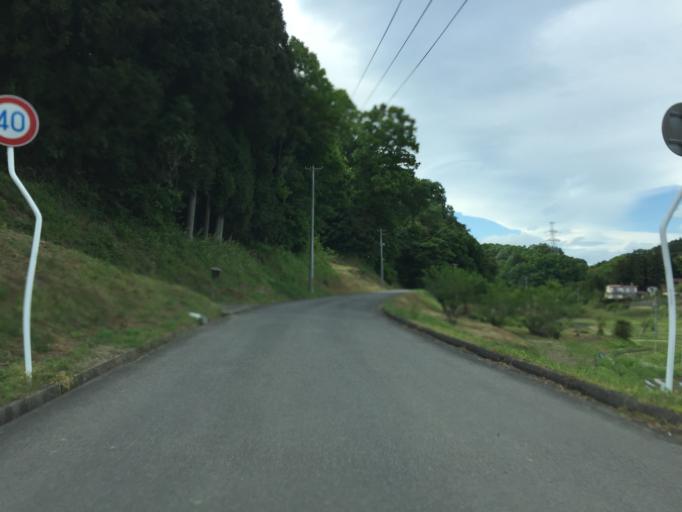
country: JP
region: Fukushima
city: Nihommatsu
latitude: 37.6247
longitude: 140.5321
